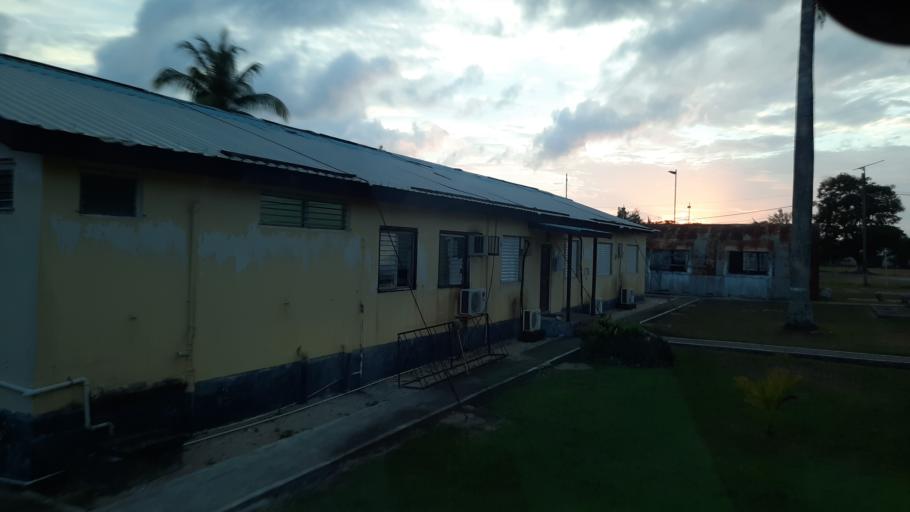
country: BZ
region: Belize
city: Belize City
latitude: 17.5426
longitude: -88.3044
